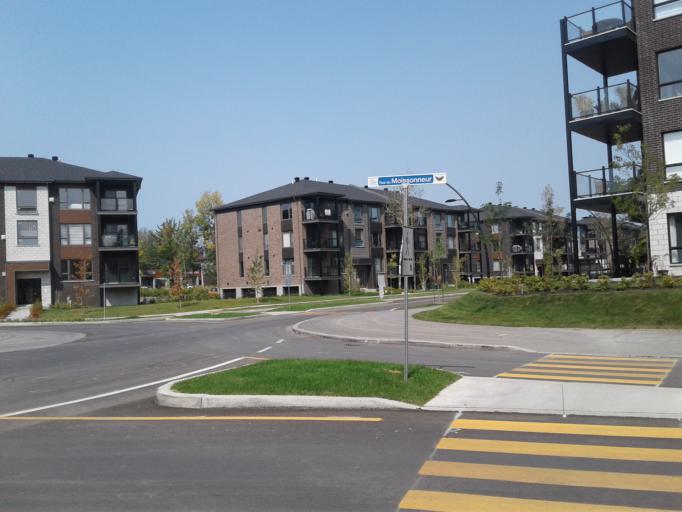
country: CA
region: Quebec
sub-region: Monteregie
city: La Prairie
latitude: 45.3968
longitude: -73.4701
